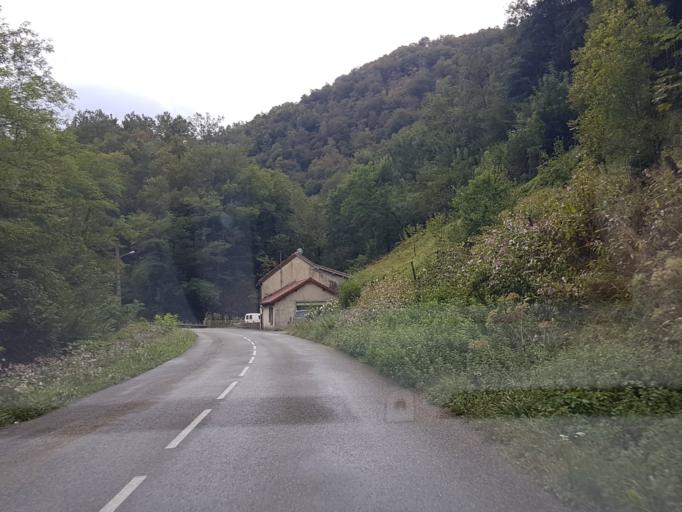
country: FR
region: Midi-Pyrenees
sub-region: Departement de l'Ariege
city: Saint-Girons
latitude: 42.9011
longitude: 1.2294
